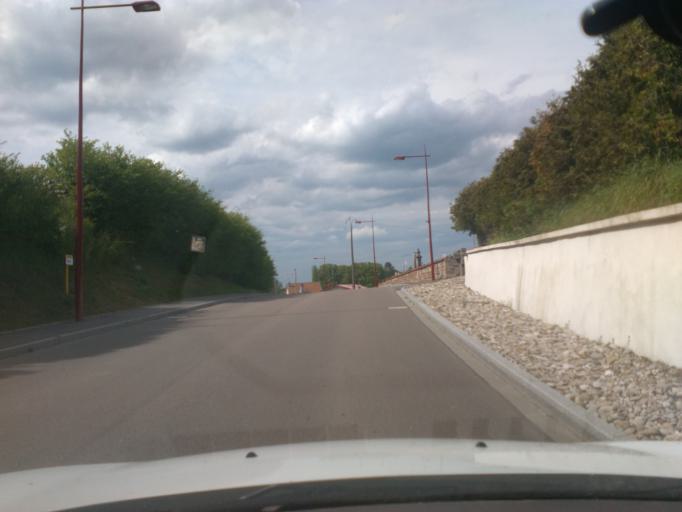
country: FR
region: Lorraine
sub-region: Departement des Vosges
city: Mirecourt
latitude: 48.2675
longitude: 6.1410
